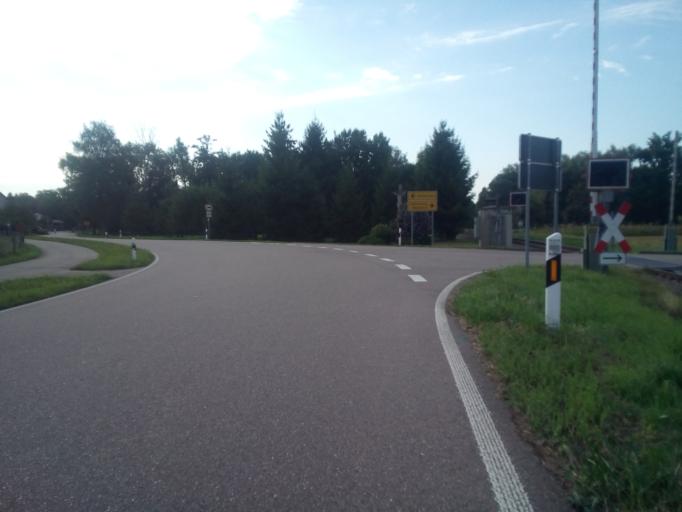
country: DE
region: Baden-Wuerttemberg
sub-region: Karlsruhe Region
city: Schwarzach
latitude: 48.7328
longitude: 8.0627
